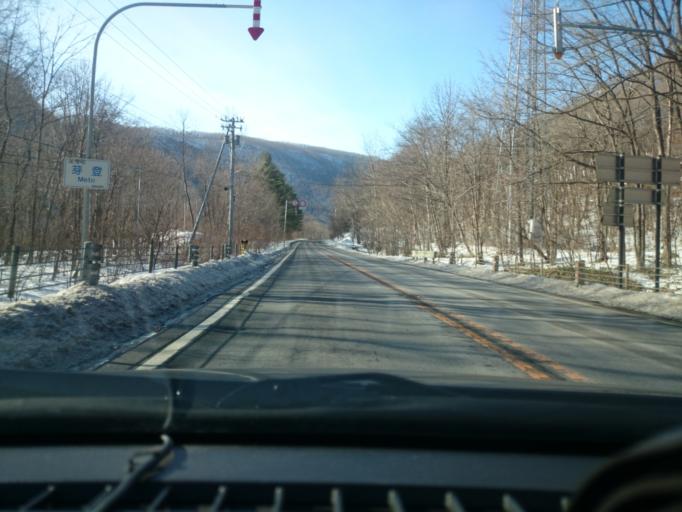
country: JP
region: Hokkaido
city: Otofuke
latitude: 43.2536
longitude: 143.4690
